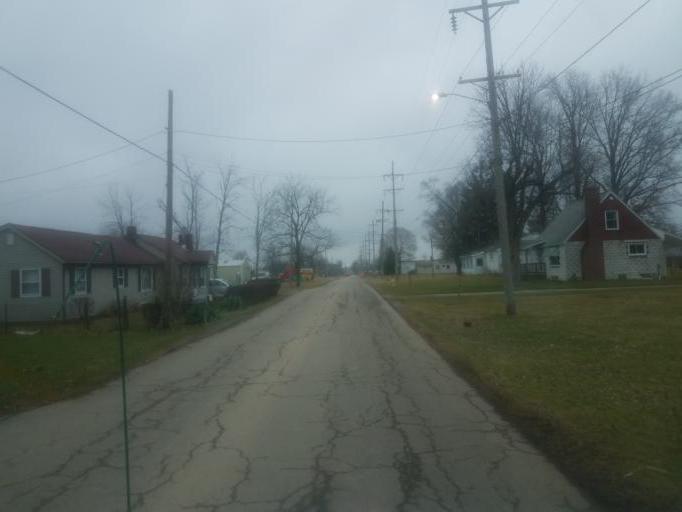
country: US
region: Ohio
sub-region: Crawford County
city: Galion
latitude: 40.7269
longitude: -82.7786
